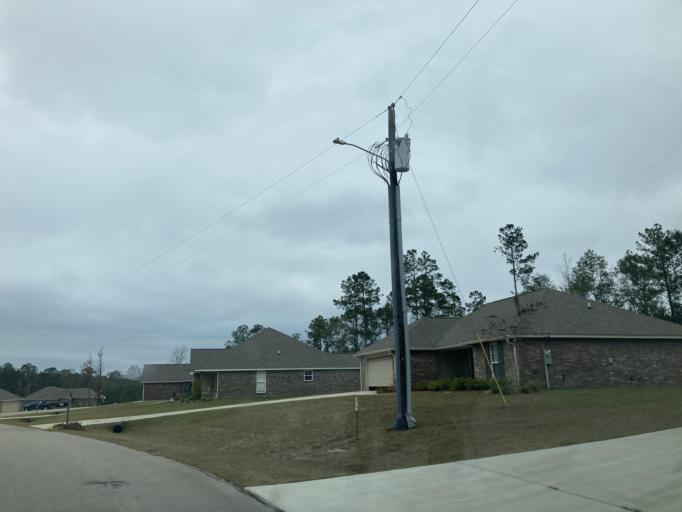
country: US
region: Mississippi
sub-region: Lamar County
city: Purvis
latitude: 31.1777
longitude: -89.4227
